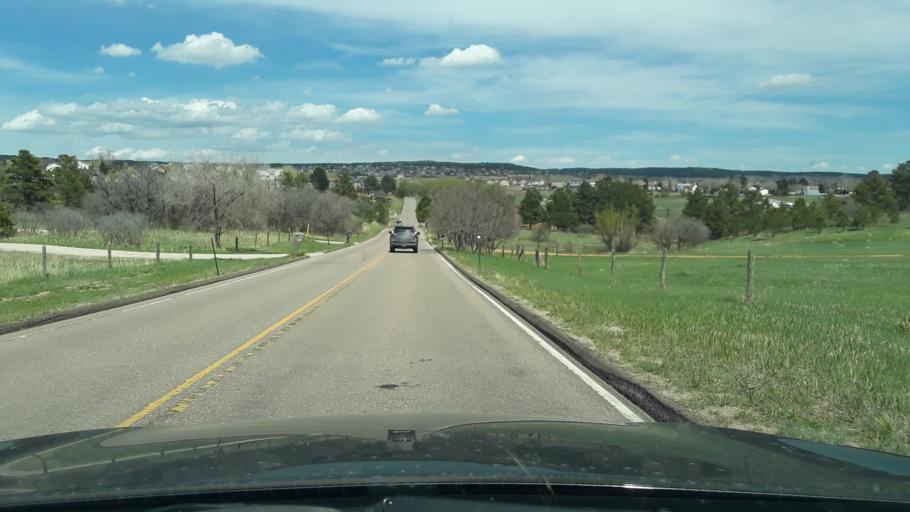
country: US
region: Colorado
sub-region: El Paso County
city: Monument
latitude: 39.0822
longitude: -104.8796
